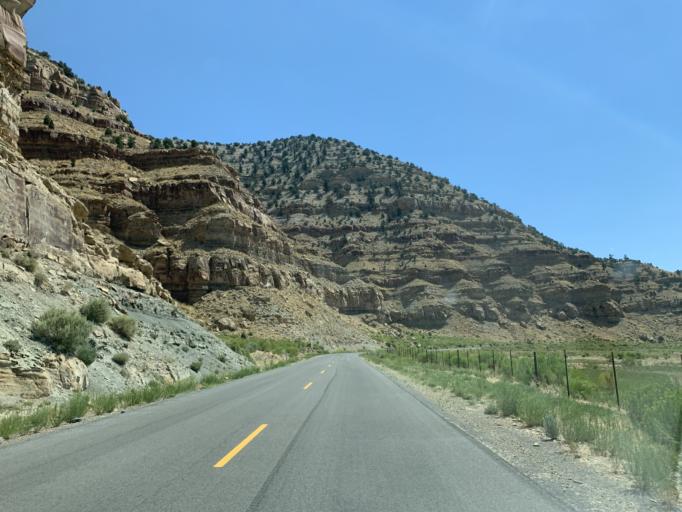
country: US
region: Utah
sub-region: Carbon County
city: East Carbon City
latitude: 39.8049
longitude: -110.3768
